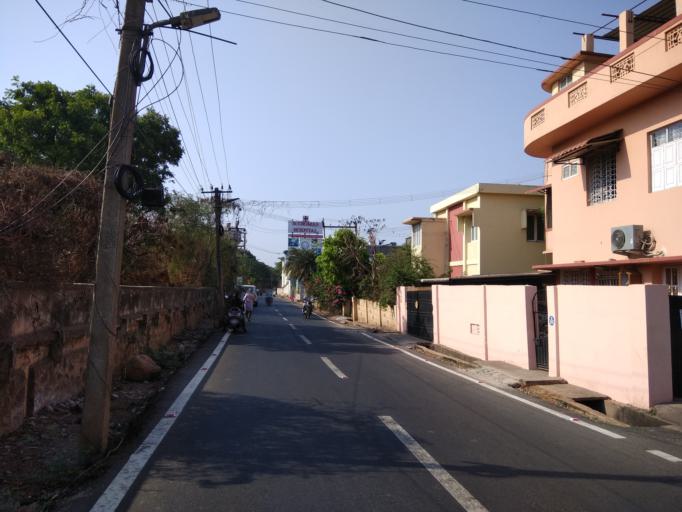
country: IN
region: Tamil Nadu
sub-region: Kancheepuram
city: Saint Thomas Mount
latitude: 13.0114
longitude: 80.1960
